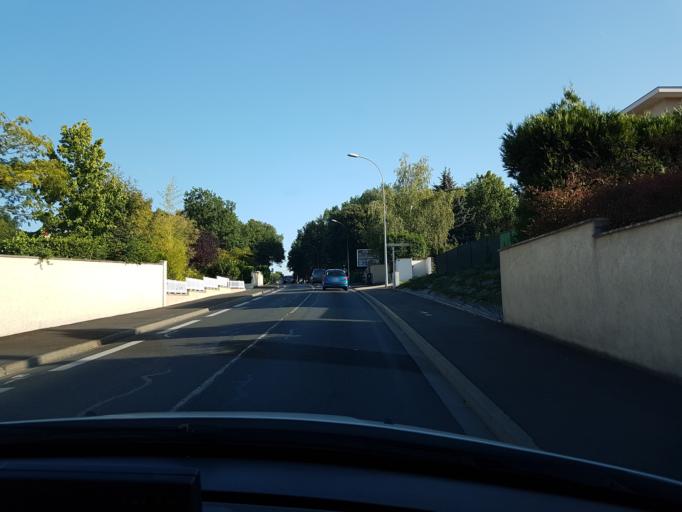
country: FR
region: Centre
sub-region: Departement d'Indre-et-Loire
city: Saint-Avertin
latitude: 47.3633
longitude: 0.7194
